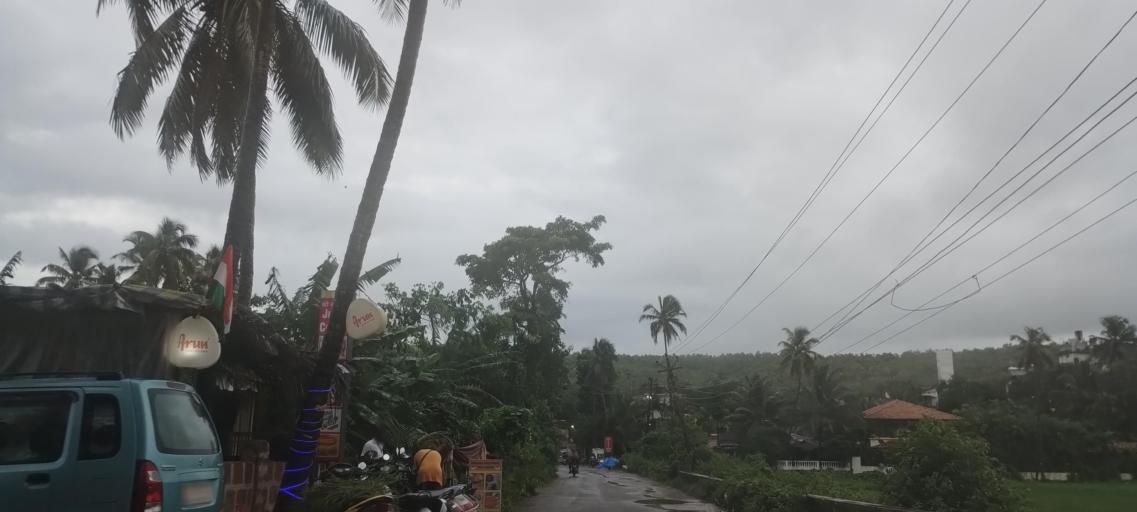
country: IN
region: Goa
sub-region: North Goa
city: Solim
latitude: 15.5963
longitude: 73.7726
